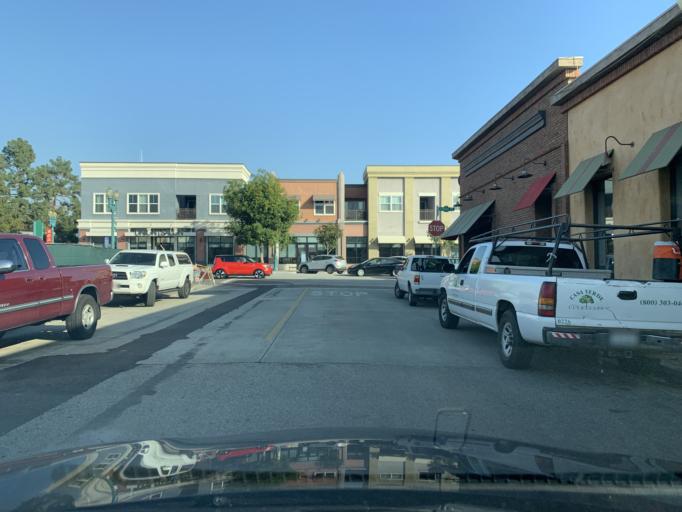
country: US
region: California
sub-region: Los Angeles County
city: Covina
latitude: 34.0892
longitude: -117.8906
